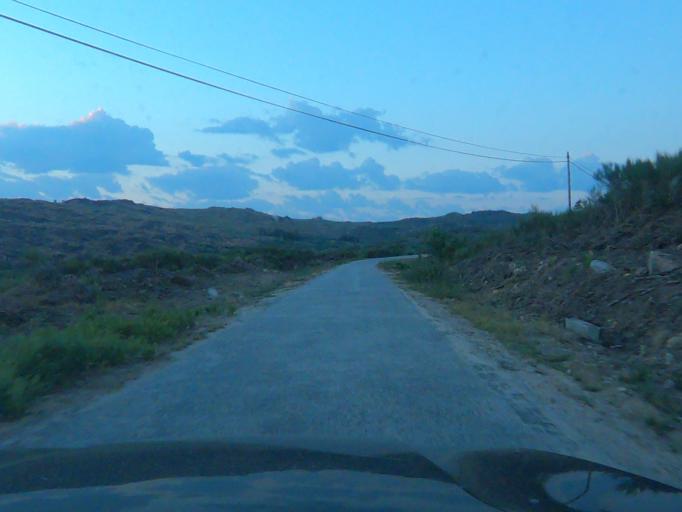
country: PT
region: Vila Real
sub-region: Sabrosa
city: Sabrosa
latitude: 41.2799
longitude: -7.6252
